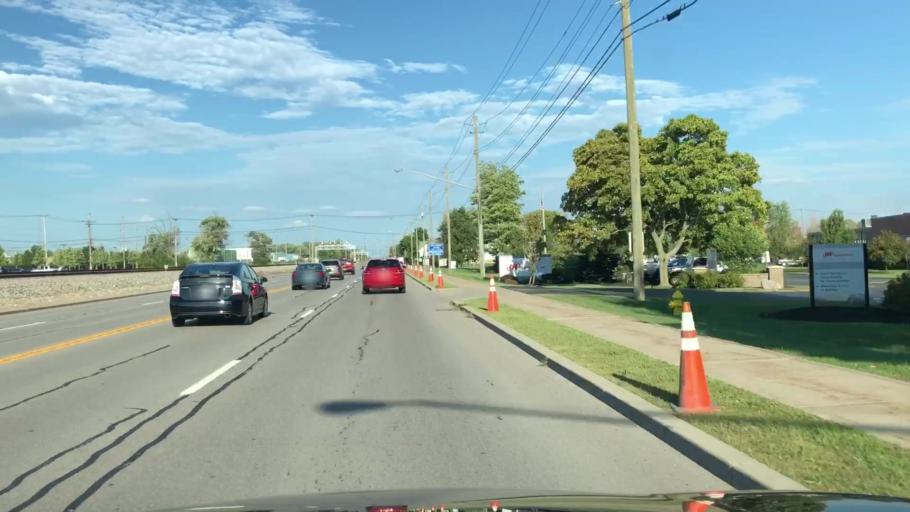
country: US
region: New York
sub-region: Erie County
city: Cheektowaga
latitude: 42.9030
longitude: -78.7623
